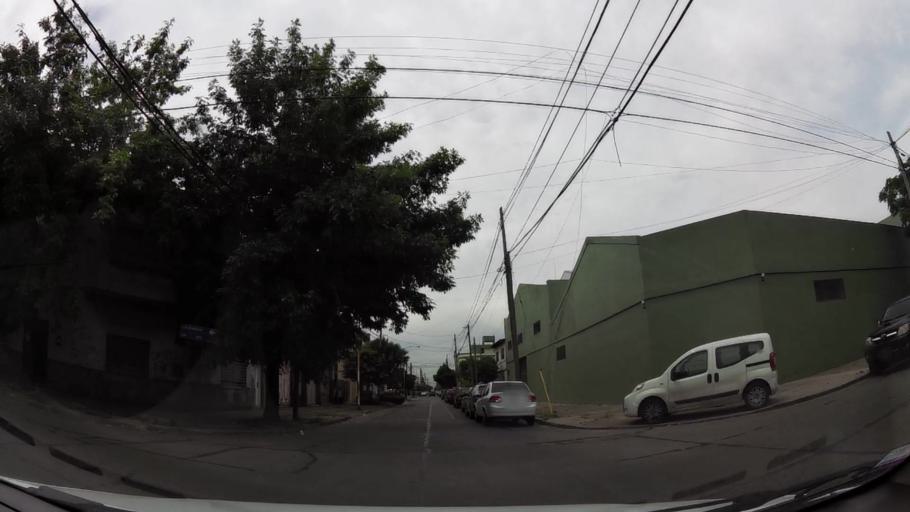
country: AR
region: Buenos Aires
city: San Justo
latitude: -34.6762
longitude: -58.5428
